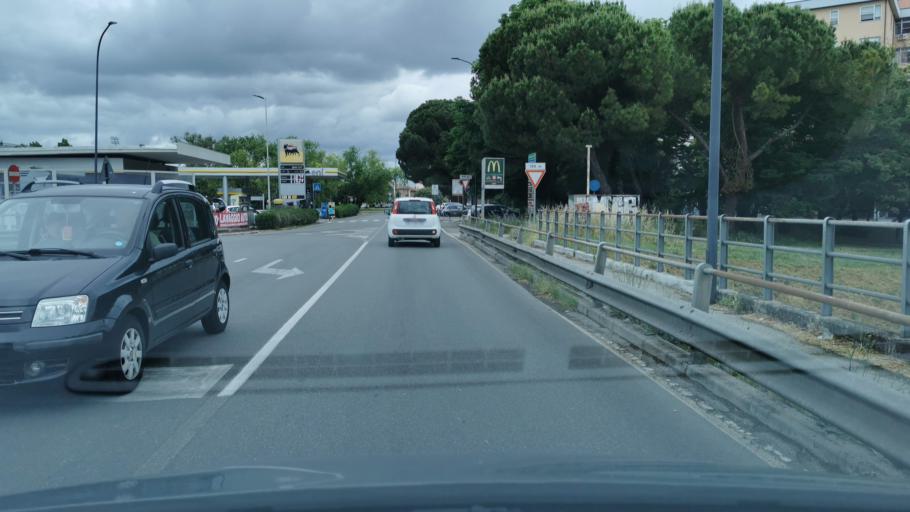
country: IT
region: Emilia-Romagna
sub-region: Provincia di Ravenna
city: Ravenna
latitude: 44.4016
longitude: 12.1969
